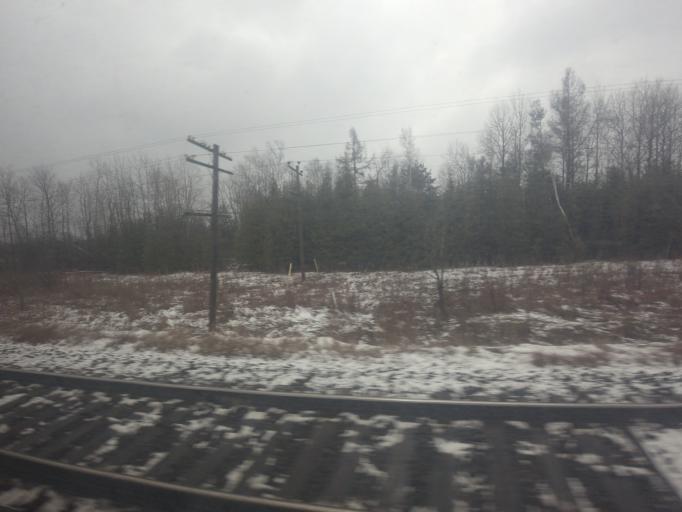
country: CA
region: Ontario
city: Quinte West
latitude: 44.0257
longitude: -77.7776
